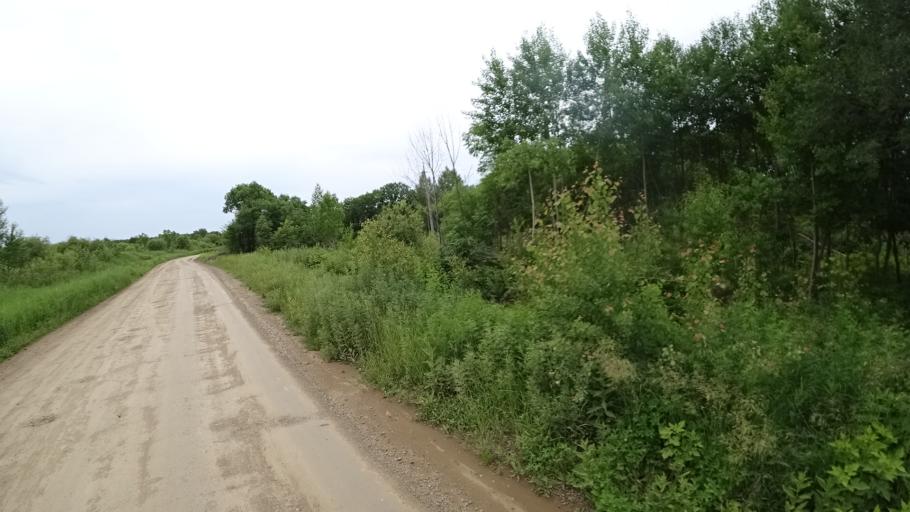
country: RU
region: Primorskiy
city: Arsen'yev
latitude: 44.1993
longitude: 133.3097
